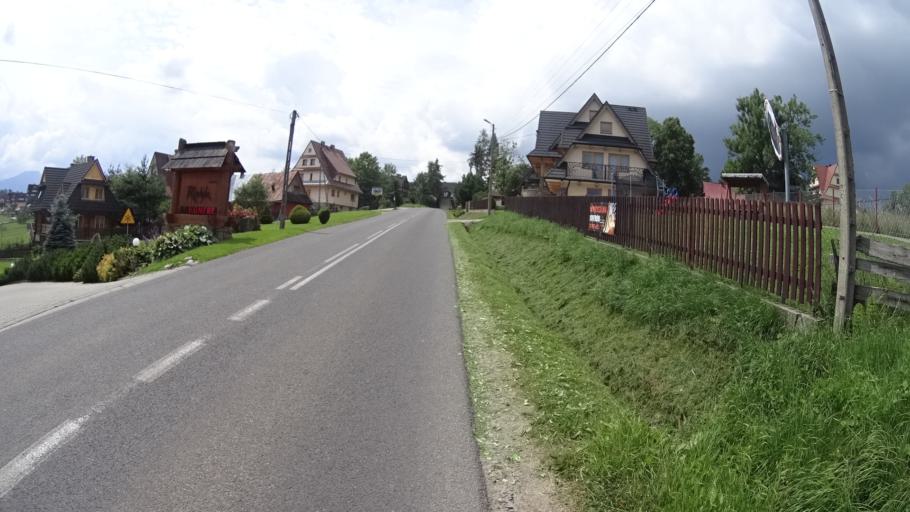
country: PL
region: Lesser Poland Voivodeship
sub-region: Powiat tatrzanski
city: Zakopane
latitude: 49.3386
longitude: 19.9513
